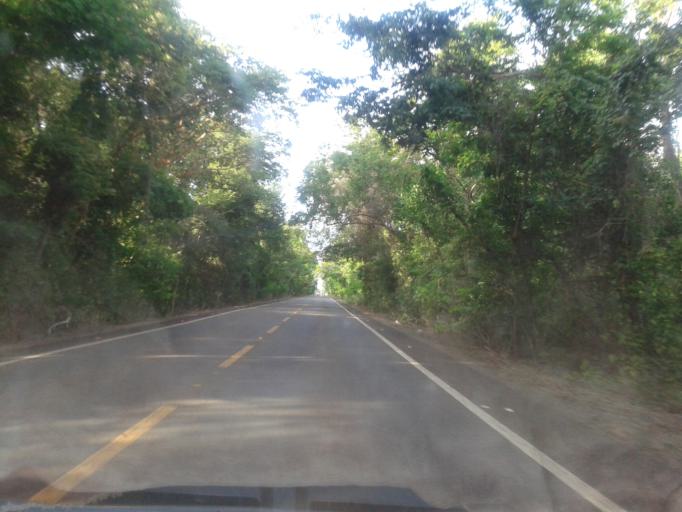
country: BR
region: Goias
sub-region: Crixas
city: Crixas
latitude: -13.9736
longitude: -50.3217
